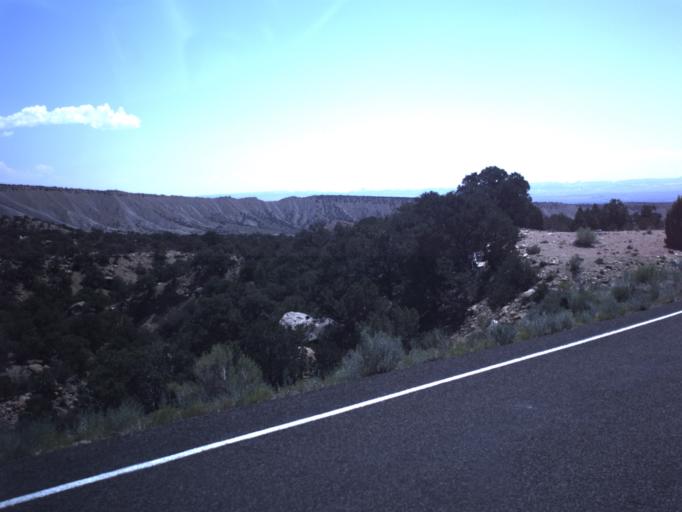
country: US
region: Utah
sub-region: Emery County
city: Orangeville
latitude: 39.3037
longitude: -111.1188
